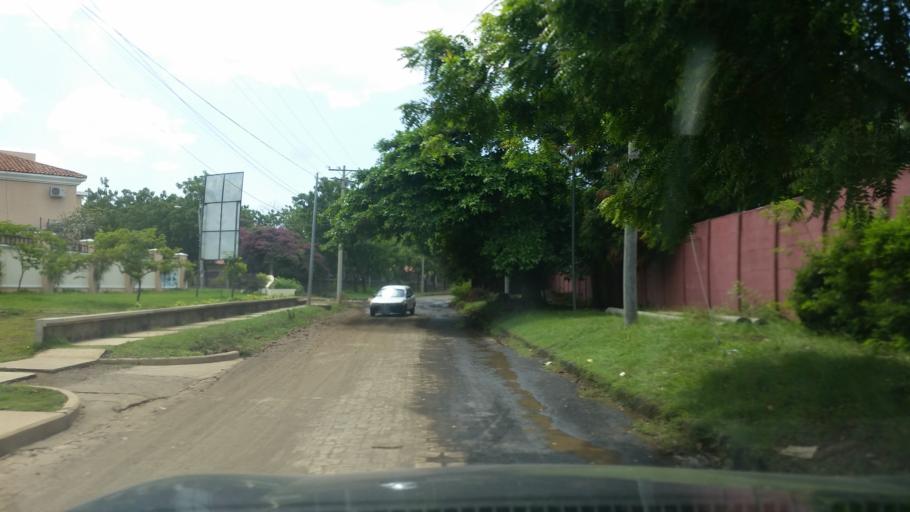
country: NI
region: Managua
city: Managua
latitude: 12.0928
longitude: -86.2236
